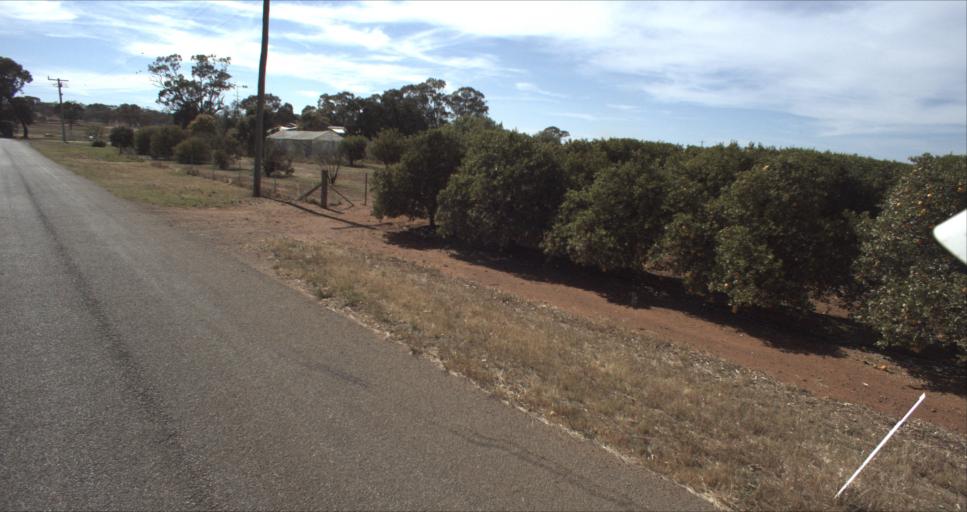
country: AU
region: New South Wales
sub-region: Leeton
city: Leeton
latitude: -34.5870
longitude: 146.4759
